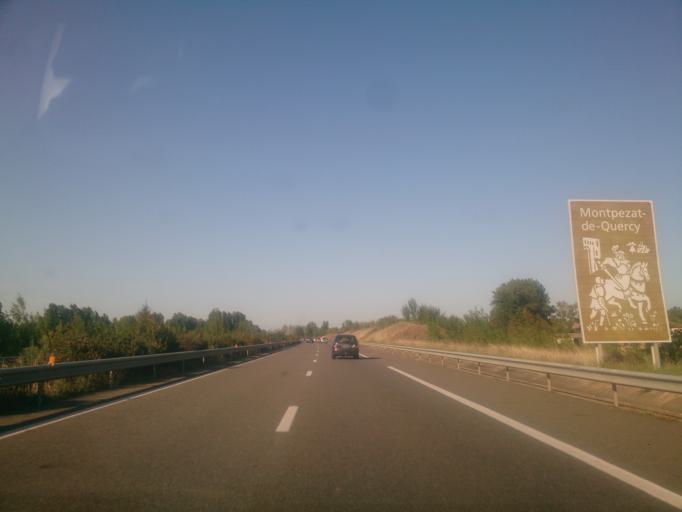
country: FR
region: Midi-Pyrenees
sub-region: Departement du Tarn-et-Garonne
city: Realville
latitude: 44.1106
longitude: 1.4661
